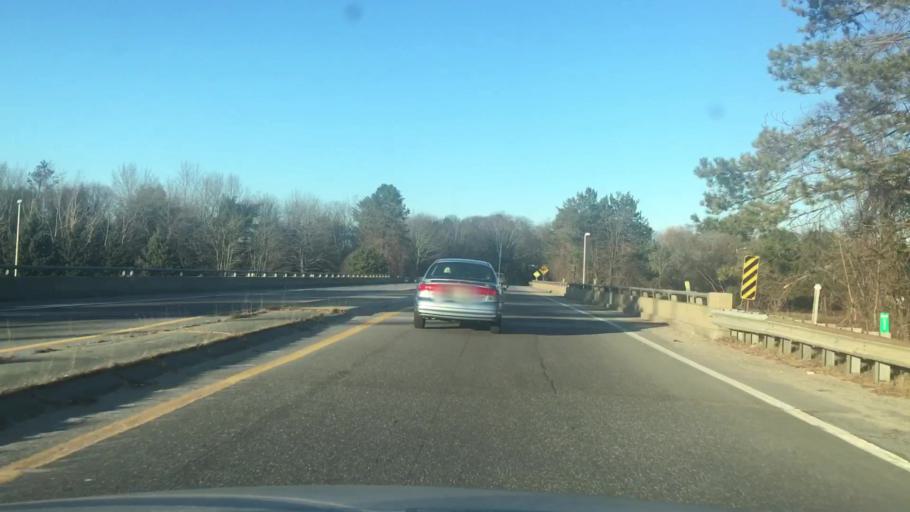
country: US
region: Maine
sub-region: Cumberland County
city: Brunswick
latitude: 43.9097
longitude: -69.9161
